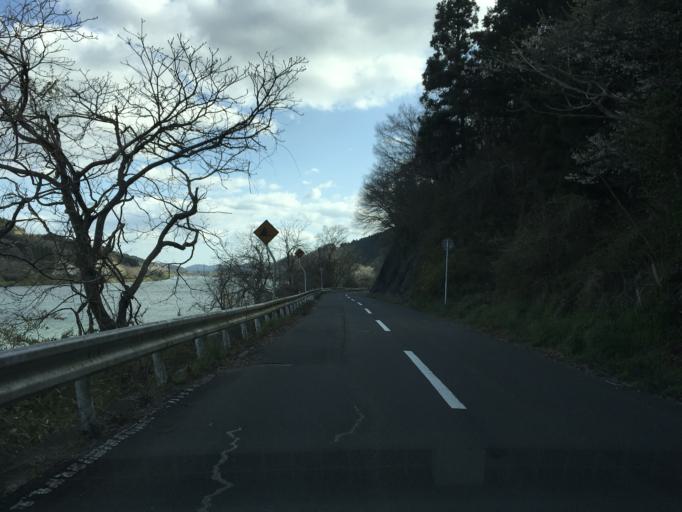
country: JP
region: Miyagi
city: Wakuya
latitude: 38.6791
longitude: 141.2846
